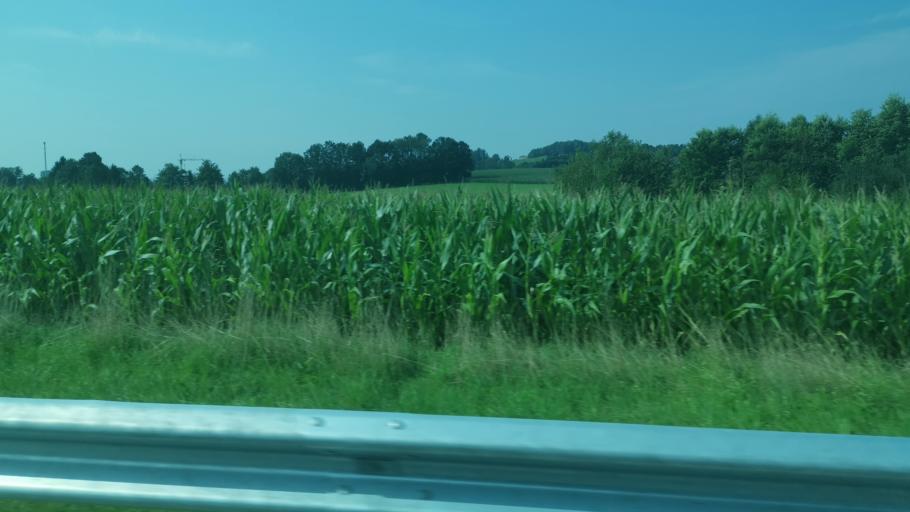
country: DE
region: Bavaria
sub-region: Upper Palatinate
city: Willmering
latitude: 49.2487
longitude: 12.6517
